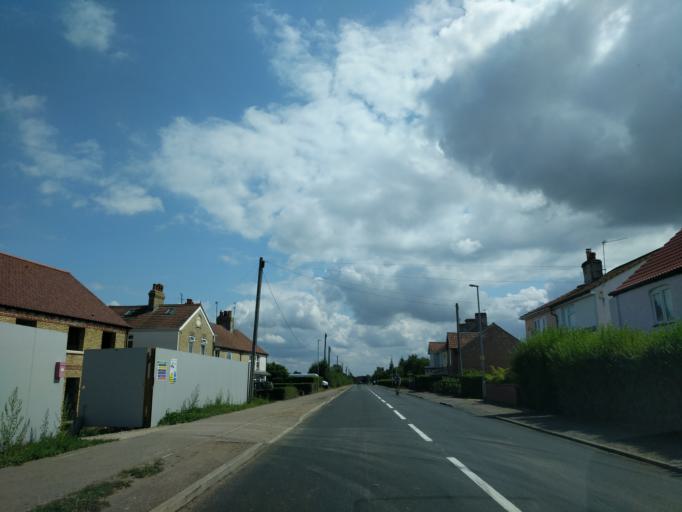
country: GB
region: England
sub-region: Cambridgeshire
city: Isleham
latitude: 52.3109
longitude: 0.3988
